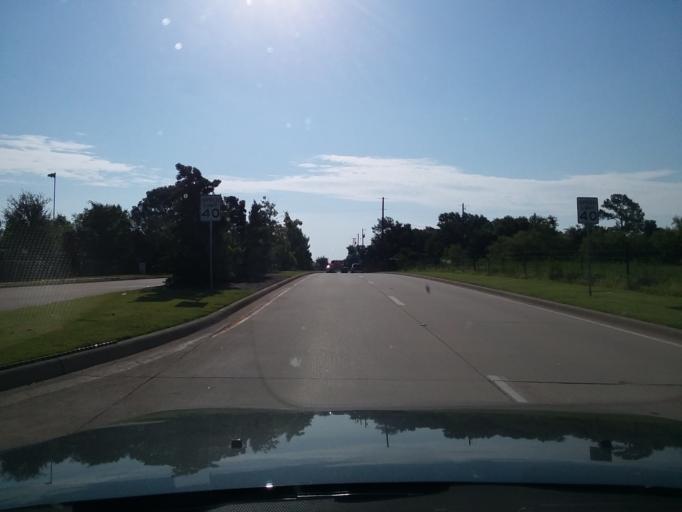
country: US
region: Texas
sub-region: Denton County
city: Highland Village
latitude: 33.0664
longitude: -97.0720
